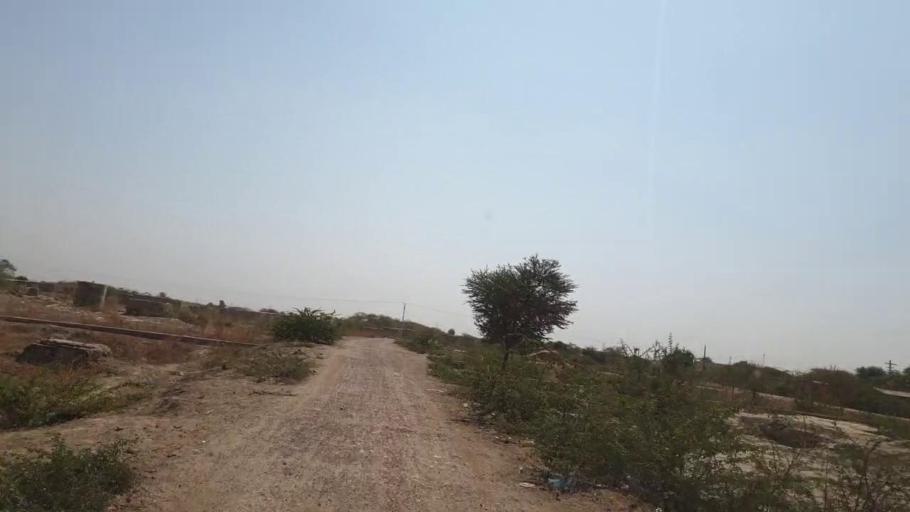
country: PK
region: Sindh
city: Kunri
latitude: 25.0847
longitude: 69.5326
